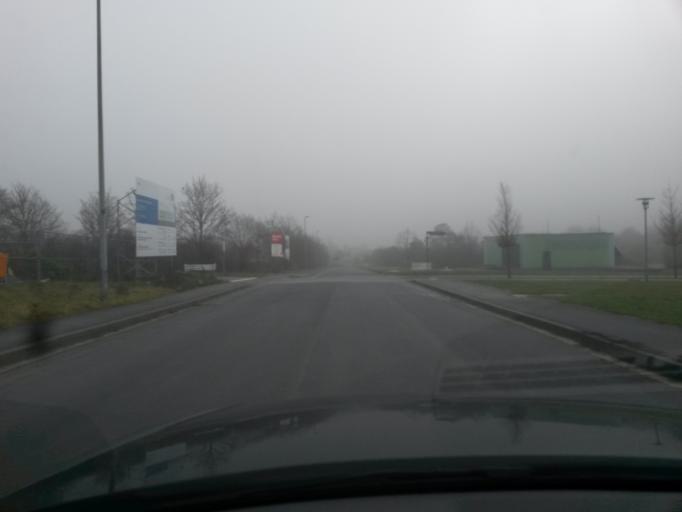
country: DE
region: Bavaria
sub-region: Regierungsbezirk Unterfranken
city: Randersacker
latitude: 49.7790
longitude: 9.9693
